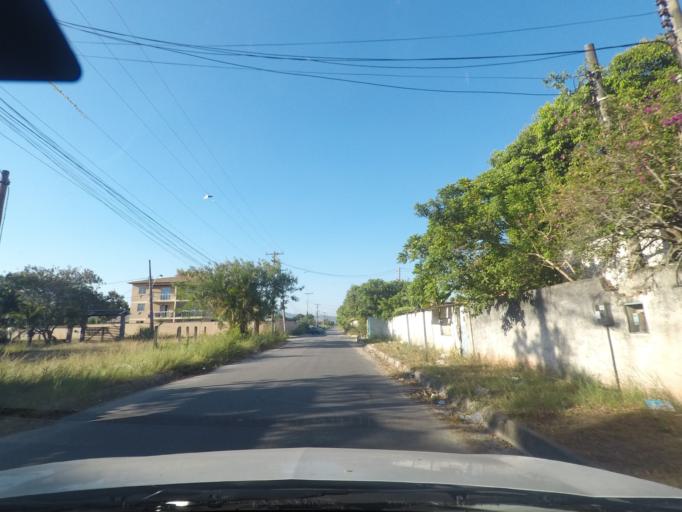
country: BR
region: Rio de Janeiro
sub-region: Marica
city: Marica
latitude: -22.9649
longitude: -42.9388
